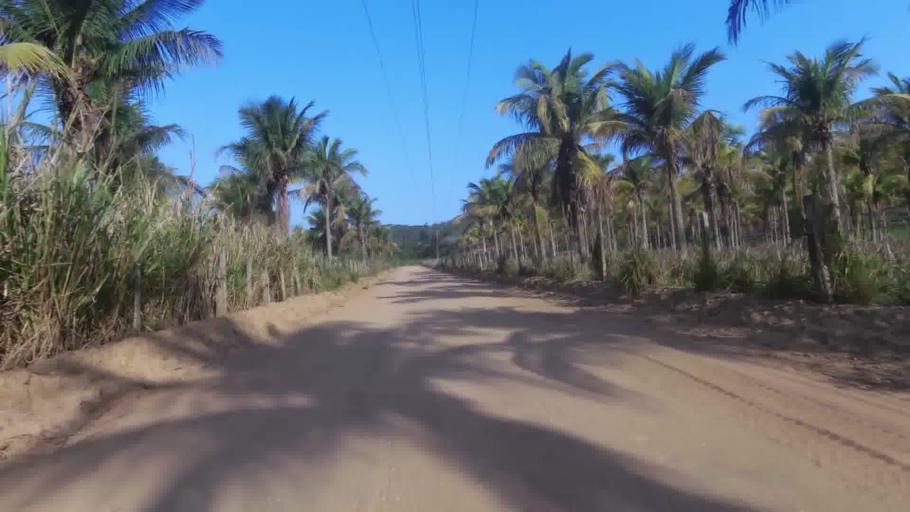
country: BR
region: Espirito Santo
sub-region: Piuma
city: Piuma
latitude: -20.8491
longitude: -40.7648
